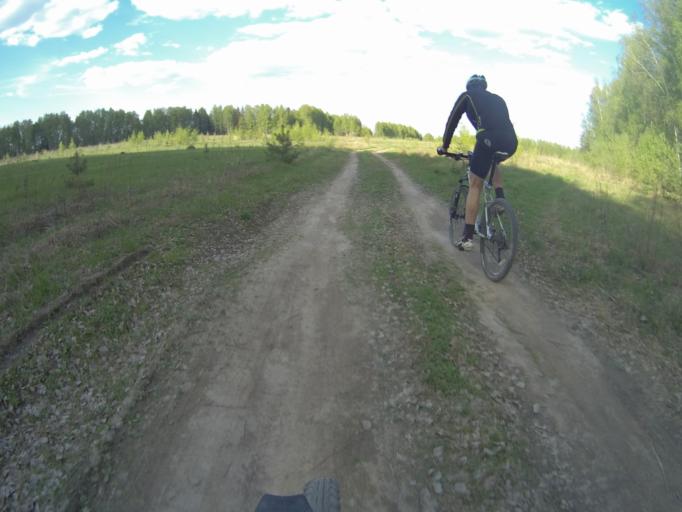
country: RU
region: Vladimir
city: Raduzhnyy
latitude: 55.9880
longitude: 40.2383
